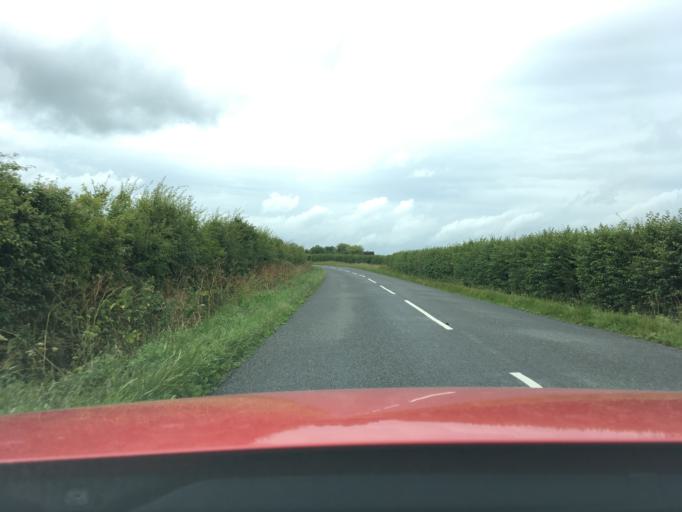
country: GB
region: England
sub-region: Worcestershire
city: Evesham
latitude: 52.0547
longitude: -1.9314
